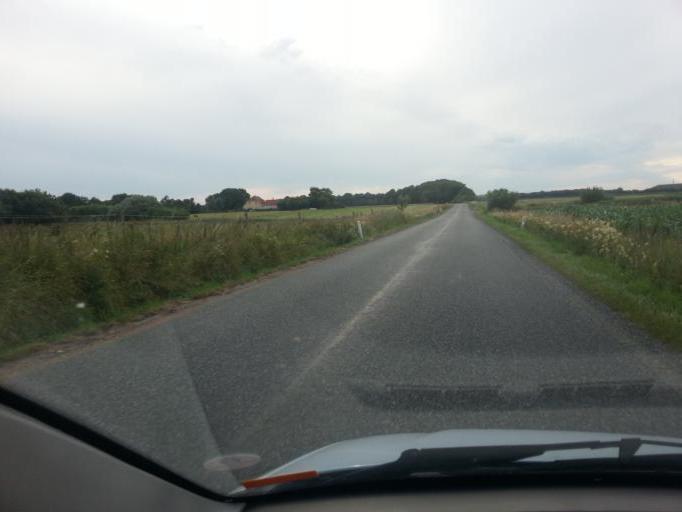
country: DK
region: South Denmark
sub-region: Vejen Kommune
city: Holsted
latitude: 55.4698
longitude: 8.8252
